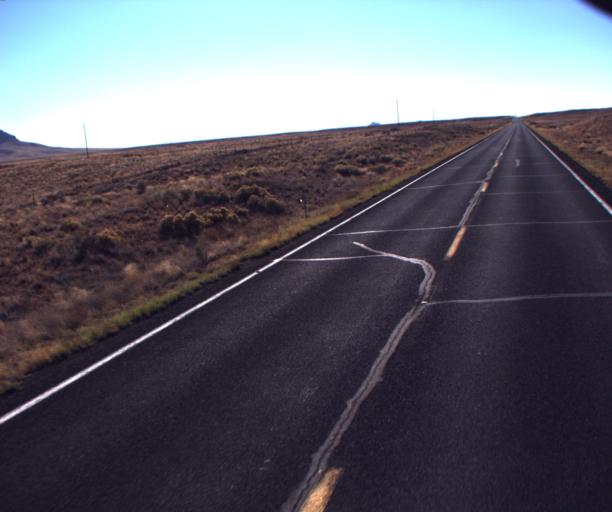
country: US
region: Arizona
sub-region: Navajo County
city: Dilkon
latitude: 35.5632
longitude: -110.4574
